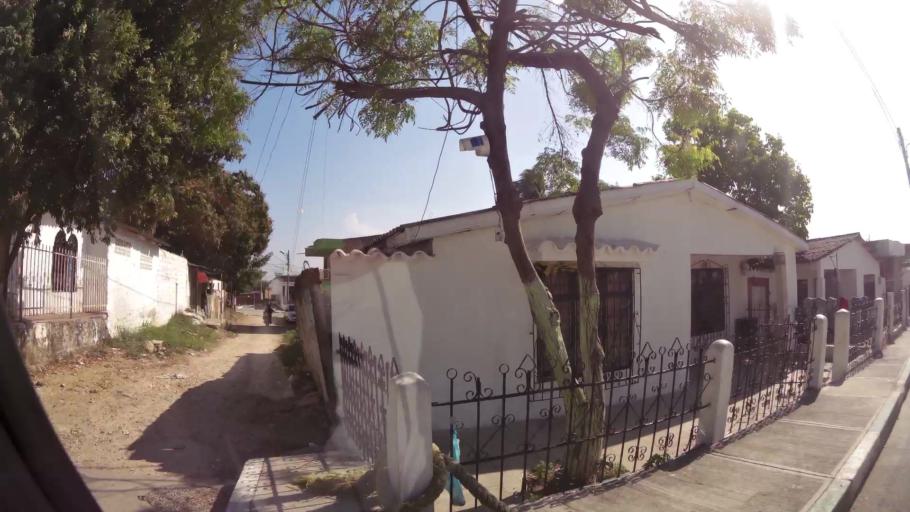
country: CO
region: Bolivar
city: Cartagena
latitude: 10.3958
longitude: -75.5022
